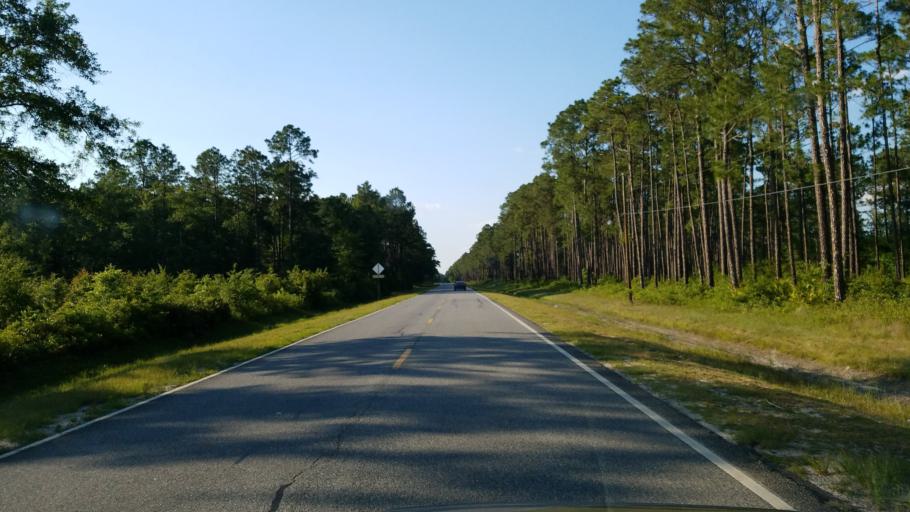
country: US
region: Georgia
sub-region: Lanier County
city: Lakeland
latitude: 30.9366
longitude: -83.0811
